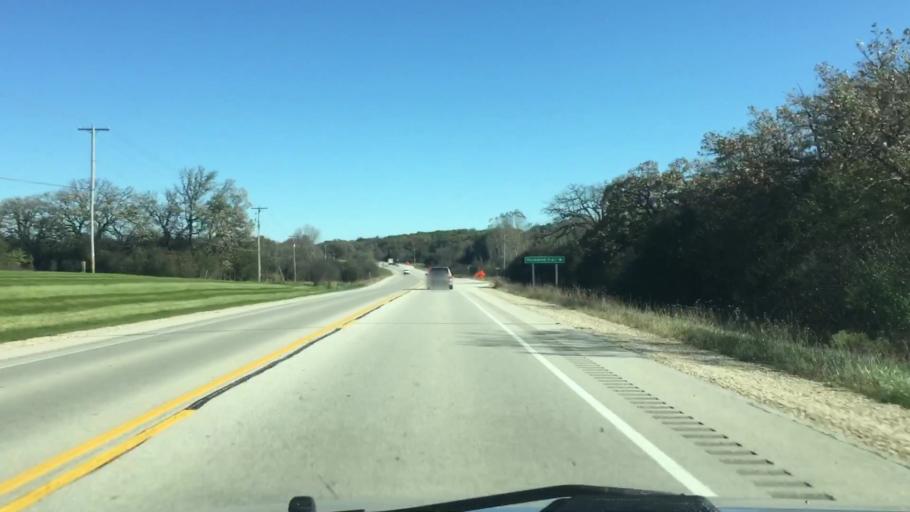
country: US
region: Wisconsin
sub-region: Waukesha County
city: Wales
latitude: 42.9623
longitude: -88.3273
